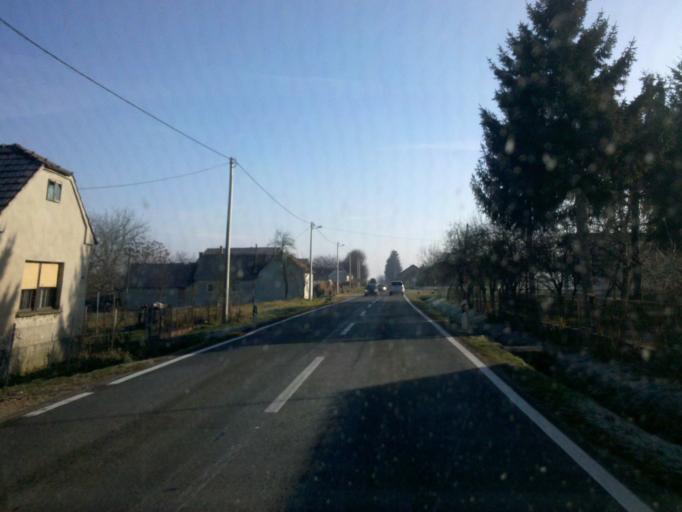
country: HR
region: Koprivnicko-Krizevacka
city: Hlebine
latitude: 46.1076
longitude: 16.9043
